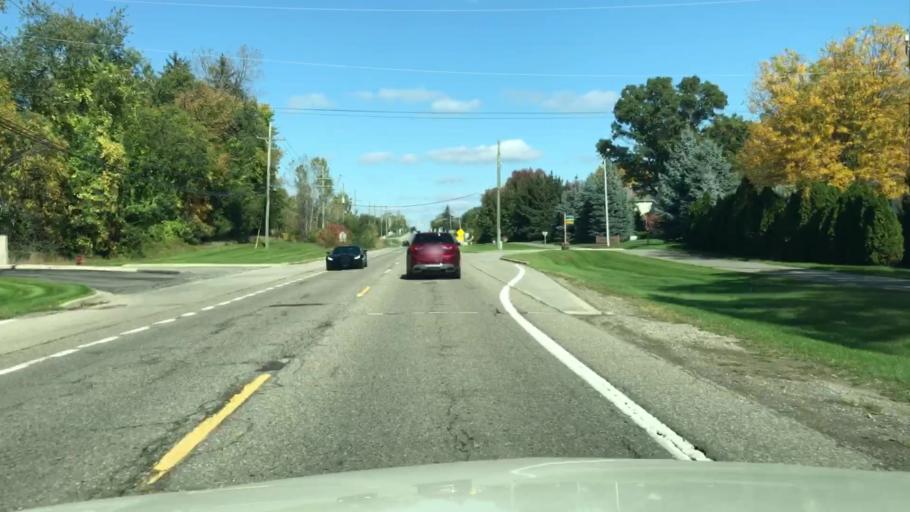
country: US
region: Michigan
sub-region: Oakland County
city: Rochester
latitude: 42.6775
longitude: -83.0939
